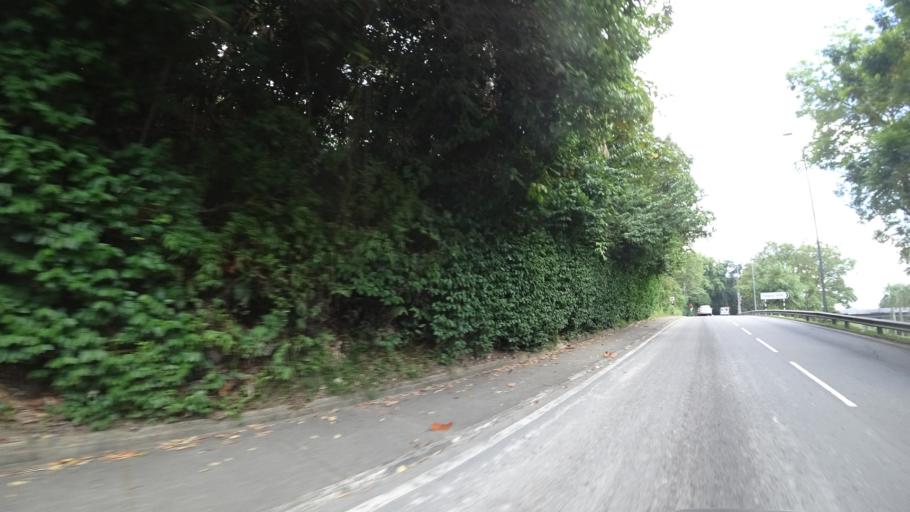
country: BN
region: Brunei and Muara
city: Bandar Seri Begawan
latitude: 4.8910
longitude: 114.9301
